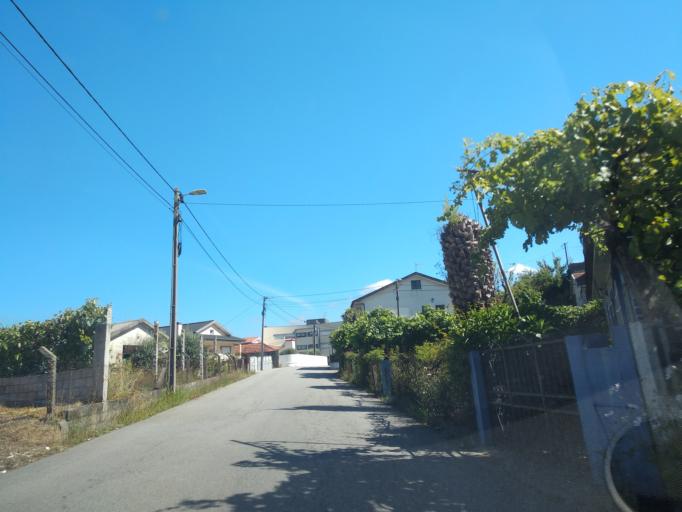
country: PT
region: Porto
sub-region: Pacos de Ferreira
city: Freamunde
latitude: 41.2761
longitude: -8.3348
